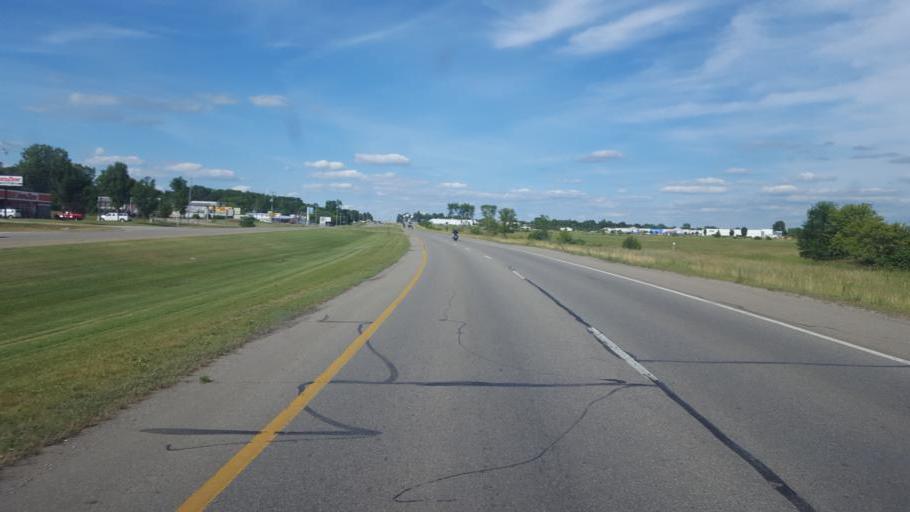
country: US
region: Michigan
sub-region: Eaton County
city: Charlotte
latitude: 42.5777
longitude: -84.8152
